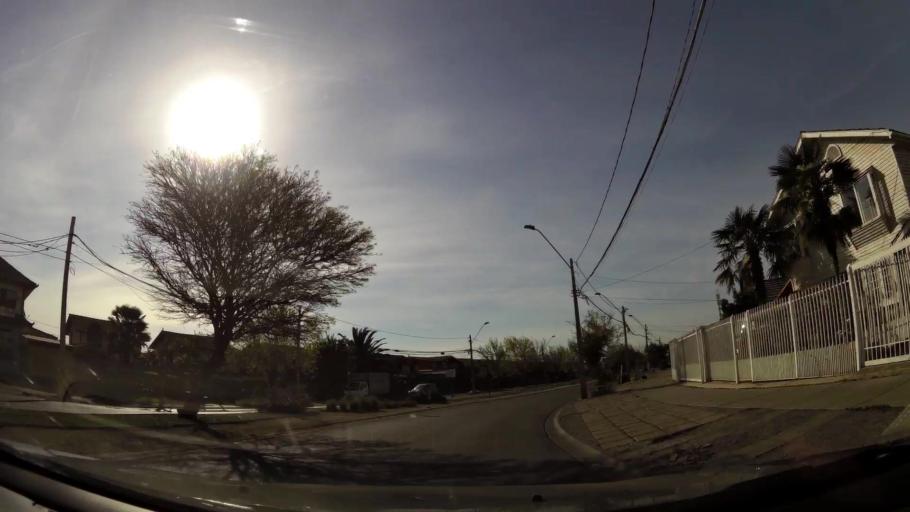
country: CL
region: Santiago Metropolitan
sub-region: Provincia de Cordillera
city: Puente Alto
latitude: -33.5881
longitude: -70.5630
